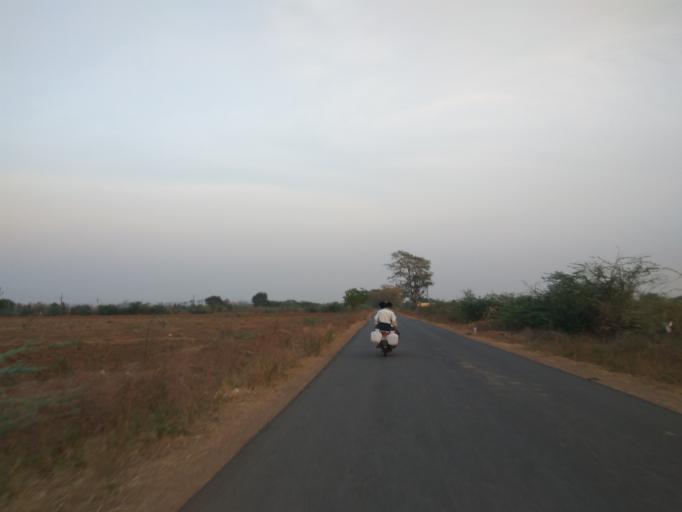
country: IN
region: Andhra Pradesh
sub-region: Prakasam
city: Markapur
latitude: 15.7510
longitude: 79.2289
